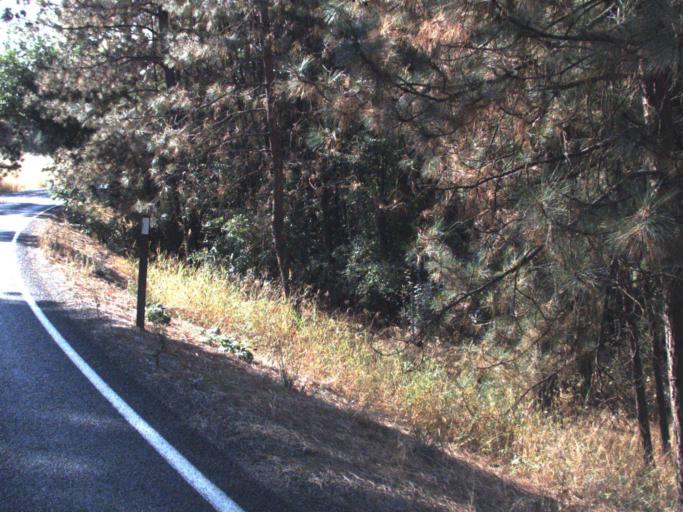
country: US
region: Washington
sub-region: Spokane County
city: Deer Park
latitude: 47.8844
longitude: -117.6577
